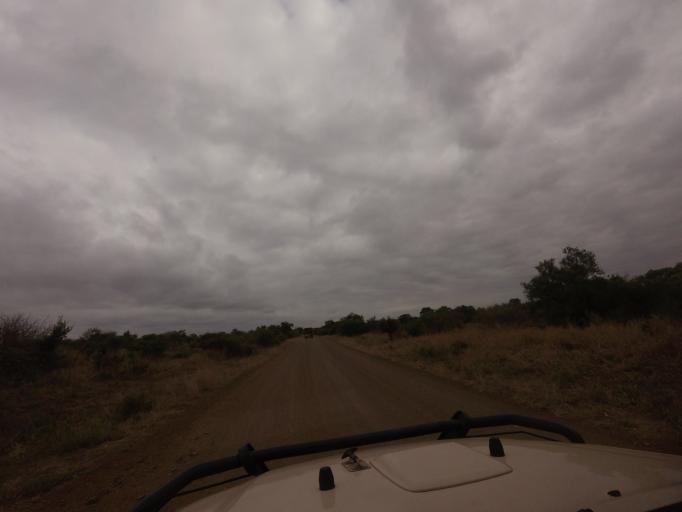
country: ZA
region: Mpumalanga
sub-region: Ehlanzeni District
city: Komatipoort
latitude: -25.1639
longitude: 31.9362
